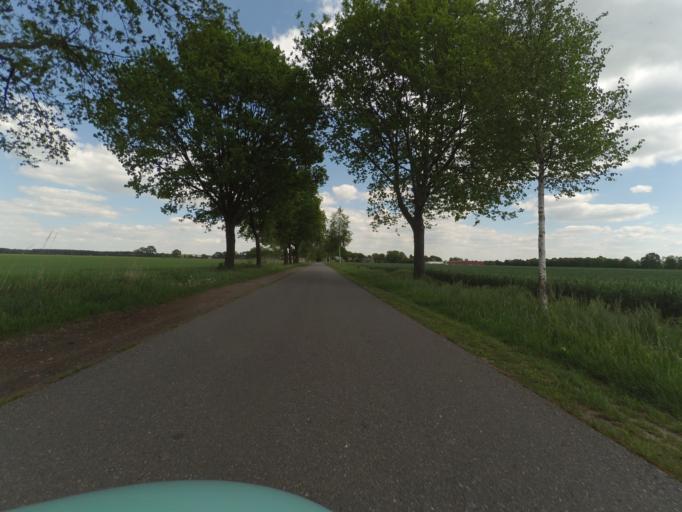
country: DE
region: Lower Saxony
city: Steinhorst
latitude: 52.6463
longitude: 10.4263
